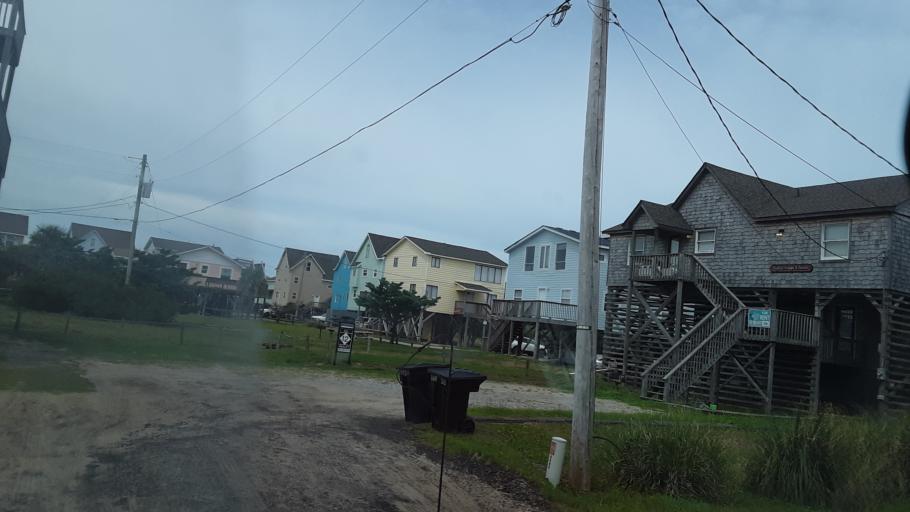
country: US
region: North Carolina
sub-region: Dare County
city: Buxton
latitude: 35.3520
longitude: -75.5013
